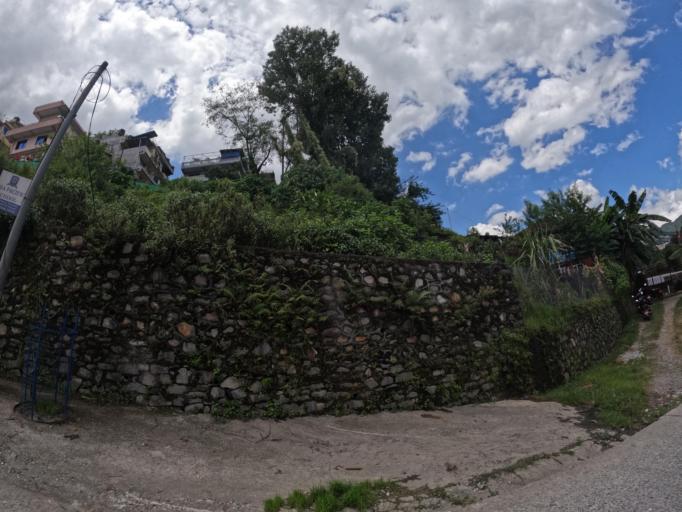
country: NP
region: Central Region
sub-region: Bagmati Zone
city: Kathmandu
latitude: 27.7703
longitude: 85.3293
